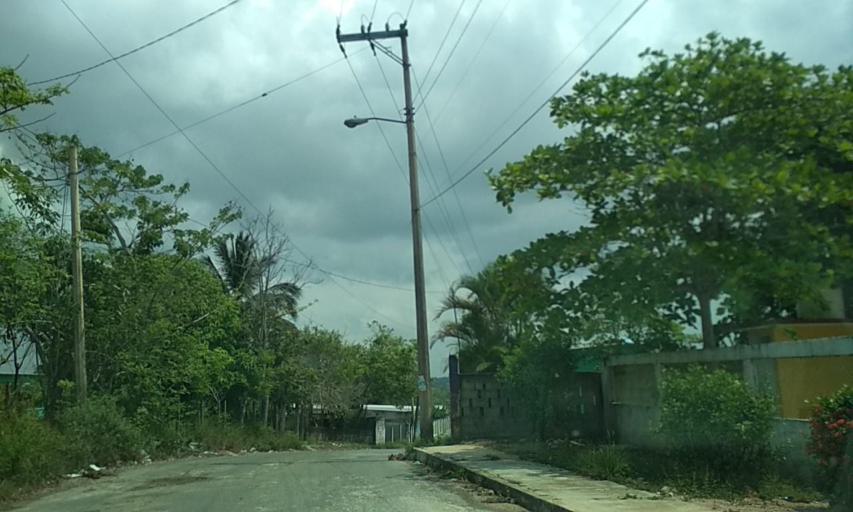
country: MX
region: Veracruz
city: Las Choapas
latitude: 17.8918
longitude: -94.1091
